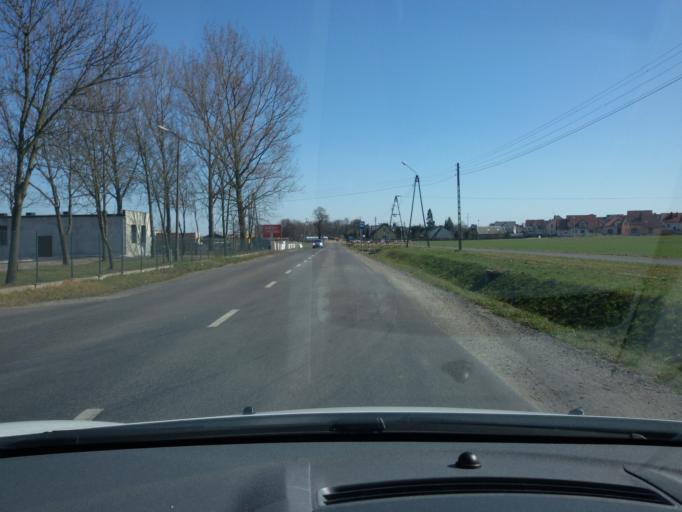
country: PL
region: Greater Poland Voivodeship
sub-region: Powiat gostynski
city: Poniec
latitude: 51.7642
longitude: 16.7906
